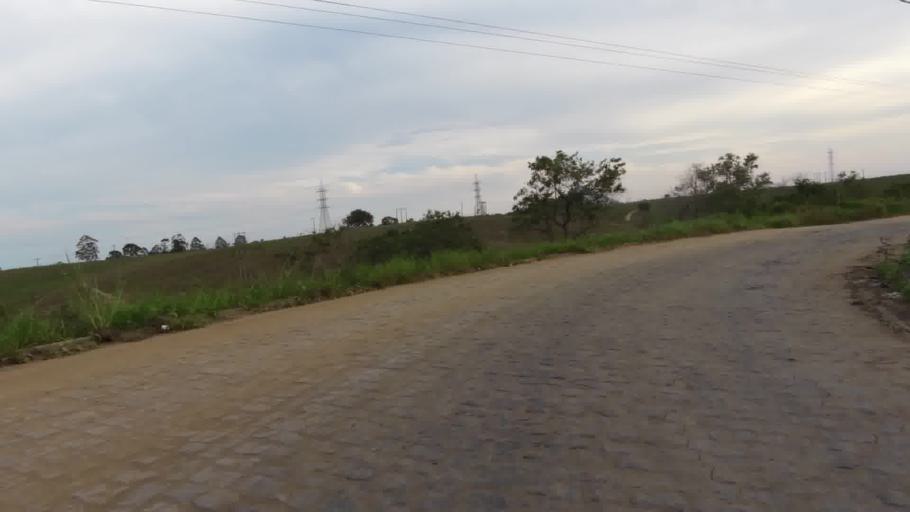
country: BR
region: Espirito Santo
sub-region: Piuma
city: Piuma
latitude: -20.8299
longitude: -40.7307
